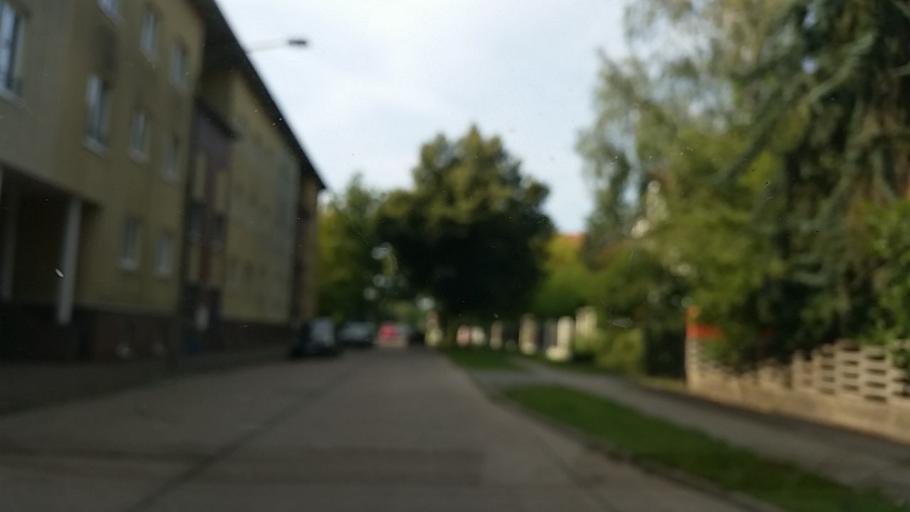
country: DE
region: Saxony-Anhalt
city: Salzwedel
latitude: 52.8443
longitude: 11.1499
